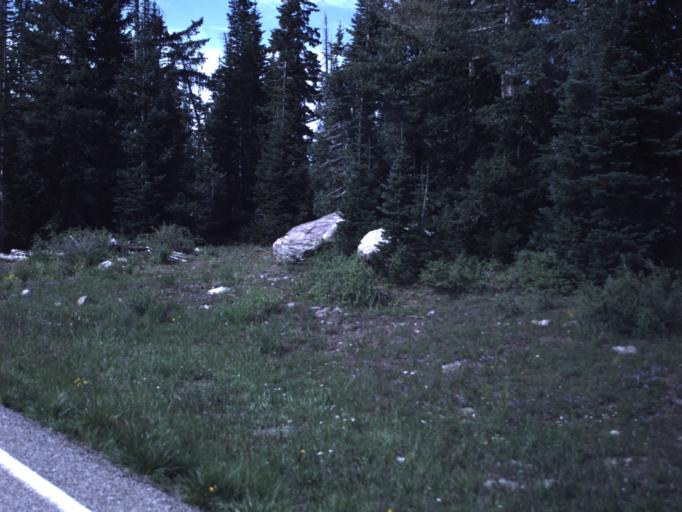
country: US
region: Utah
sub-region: Iron County
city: Cedar City
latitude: 37.5984
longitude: -112.8501
